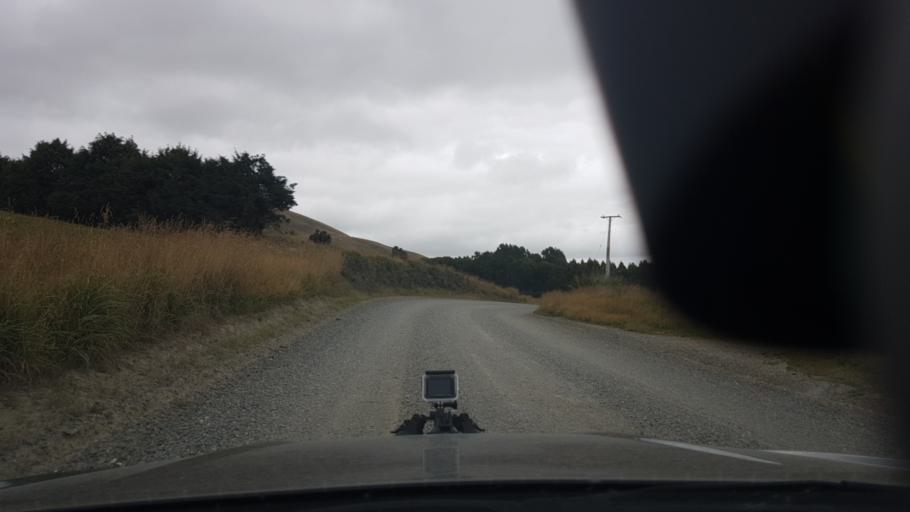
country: NZ
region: Otago
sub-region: Clutha District
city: Papatowai
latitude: -46.3178
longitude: 169.3620
